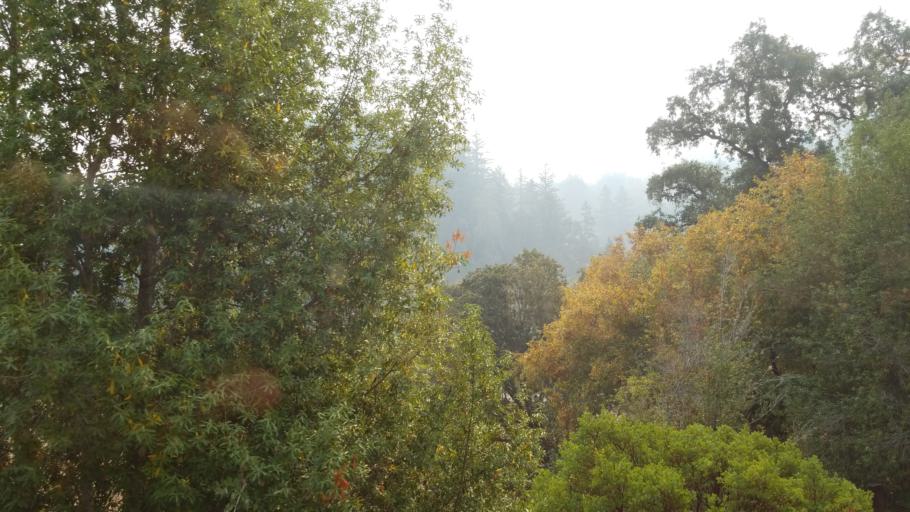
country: US
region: California
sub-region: Mendocino County
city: Willits
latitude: 39.4043
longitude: -123.3886
